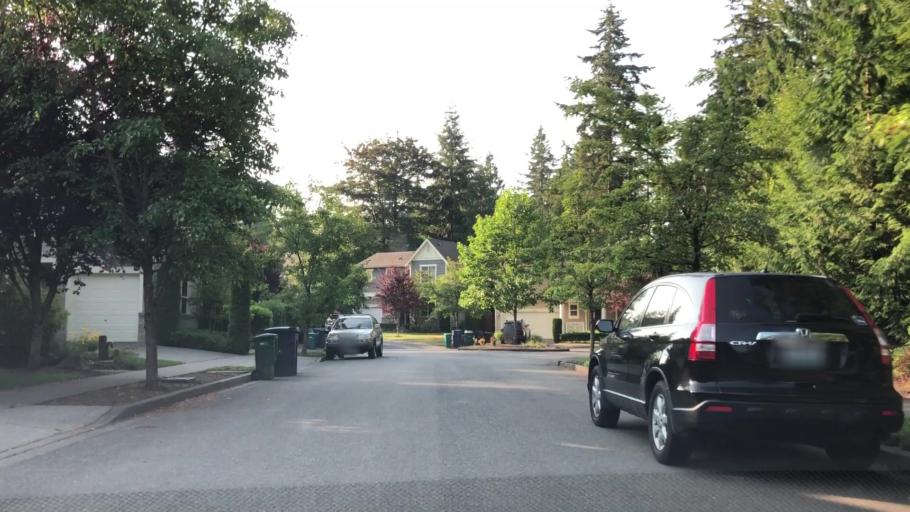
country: US
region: Washington
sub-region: King County
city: Union Hill-Novelty Hill
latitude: 47.6759
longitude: -122.0279
